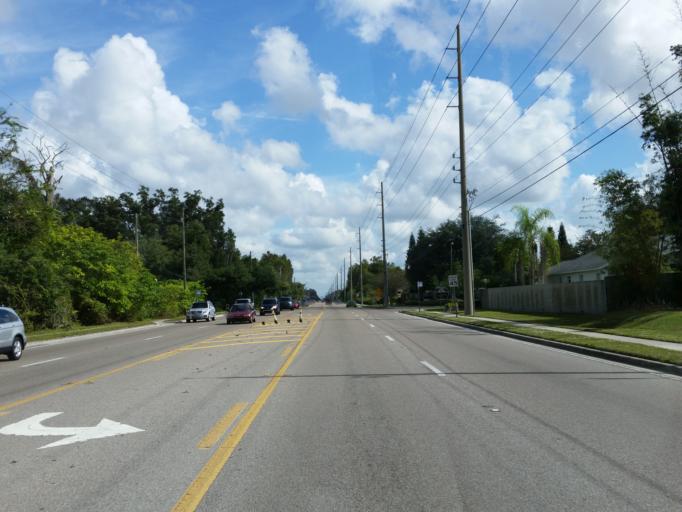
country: US
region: Florida
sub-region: Hillsborough County
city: Riverview
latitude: 27.8936
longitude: -82.3263
